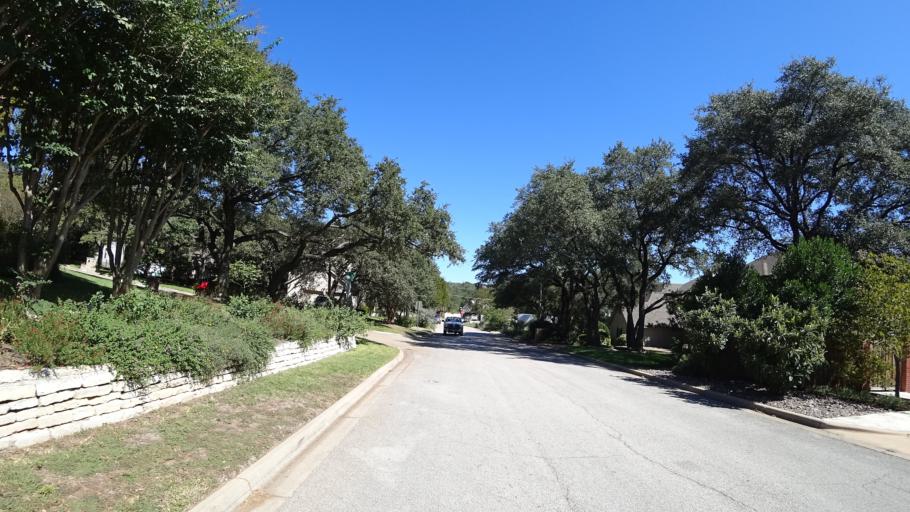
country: US
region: Texas
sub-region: Travis County
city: West Lake Hills
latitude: 30.3386
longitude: -97.7785
